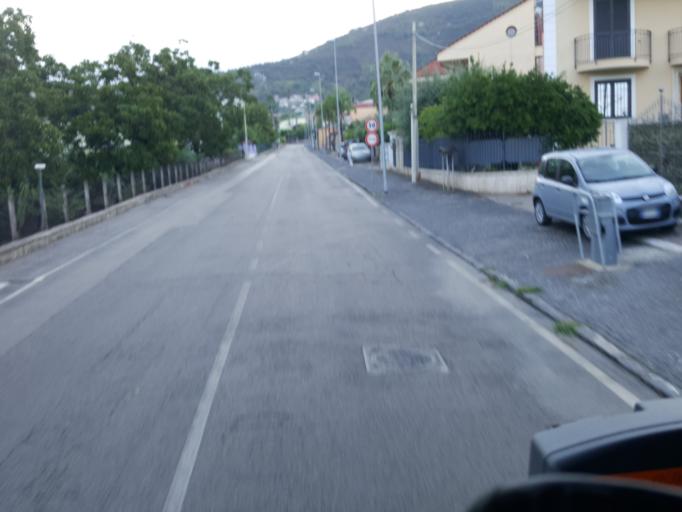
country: IT
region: Campania
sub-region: Provincia di Napoli
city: Carbonara di Nola
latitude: 40.8813
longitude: 14.5726
